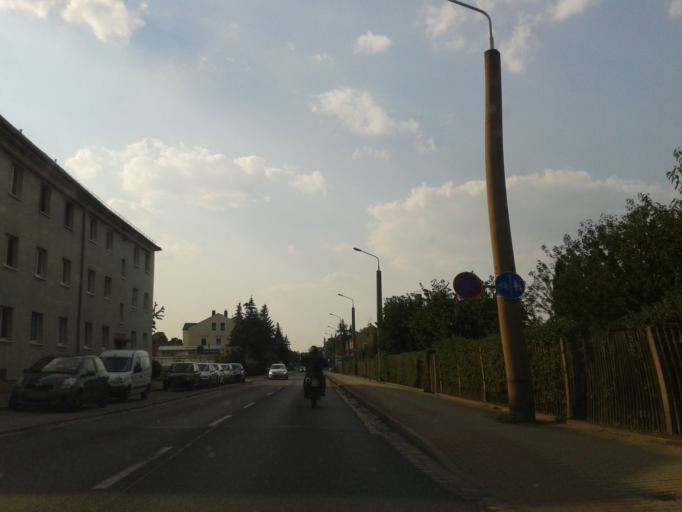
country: DE
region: Saxony
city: Radebeul
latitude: 51.0798
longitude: 13.6588
